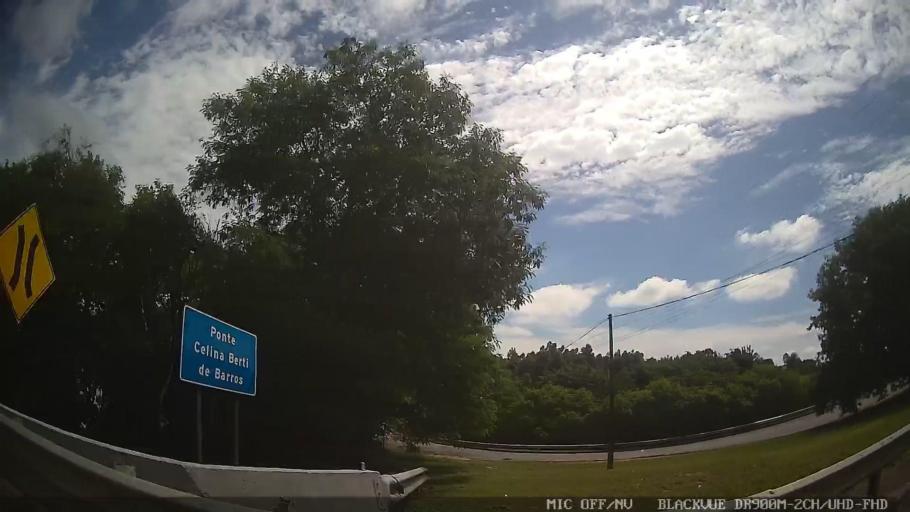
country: BR
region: Sao Paulo
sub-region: Laranjal Paulista
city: Laranjal Paulista
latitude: -23.0652
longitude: -47.8201
